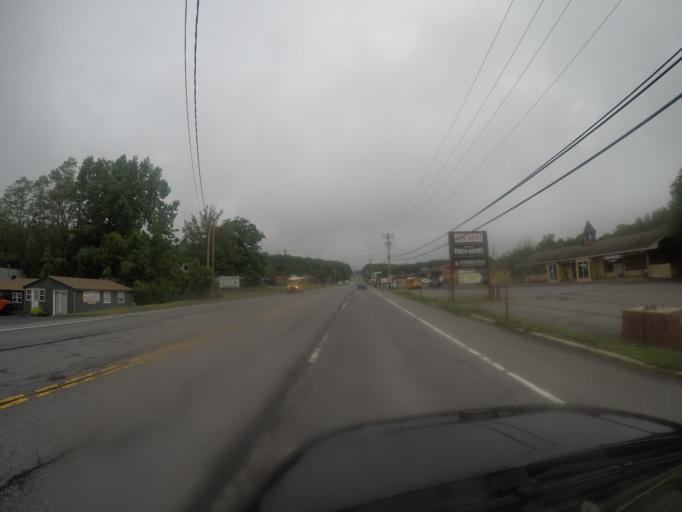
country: US
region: New York
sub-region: Ulster County
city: West Hurley
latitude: 41.9818
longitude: -74.0861
